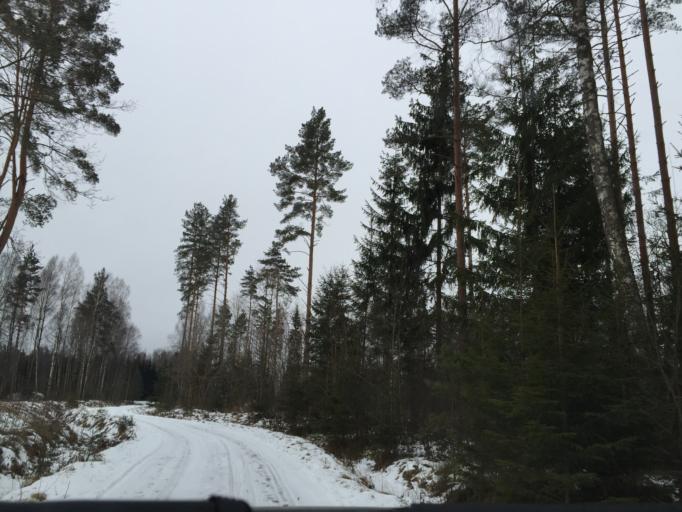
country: LV
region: Saulkrastu
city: Saulkrasti
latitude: 57.2412
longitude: 24.5074
